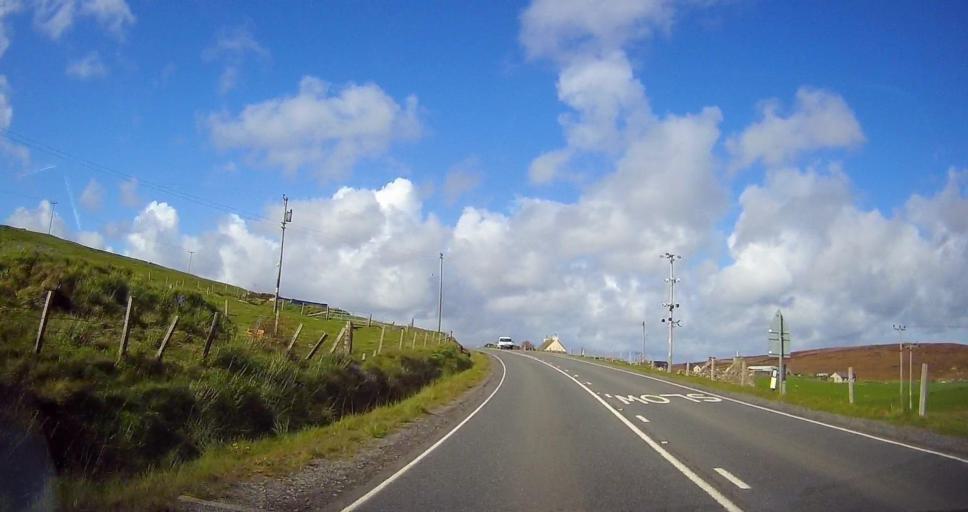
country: GB
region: Scotland
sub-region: Shetland Islands
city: Lerwick
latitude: 60.2368
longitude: -1.2313
